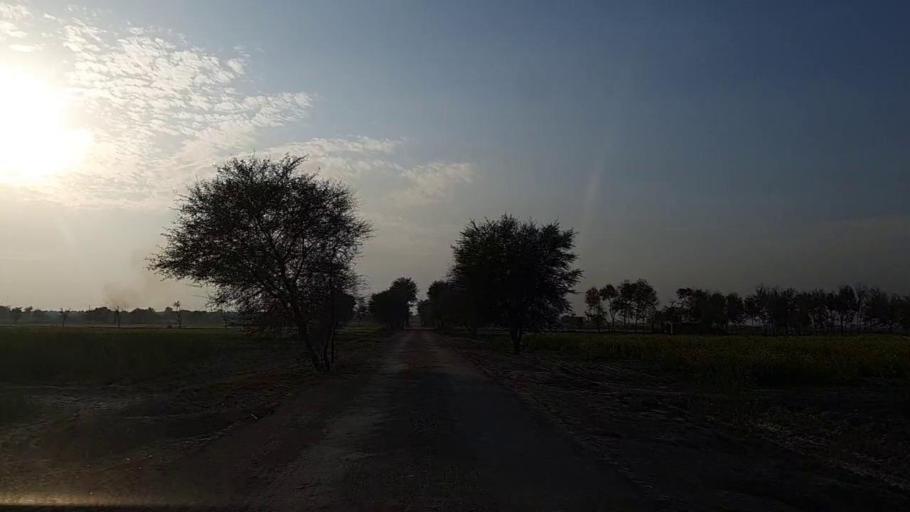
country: PK
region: Sindh
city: Jam Sahib
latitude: 26.3945
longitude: 68.5125
